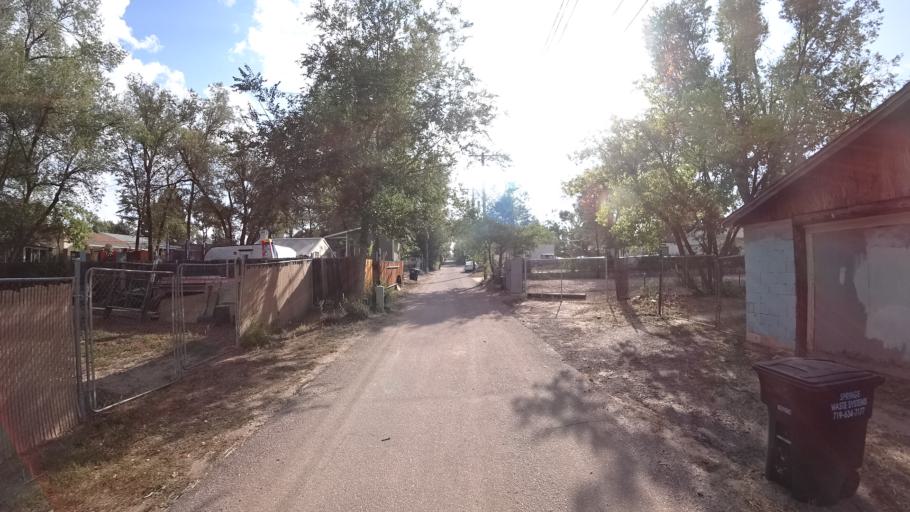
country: US
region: Colorado
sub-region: El Paso County
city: Colorado Springs
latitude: 38.8257
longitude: -104.8073
